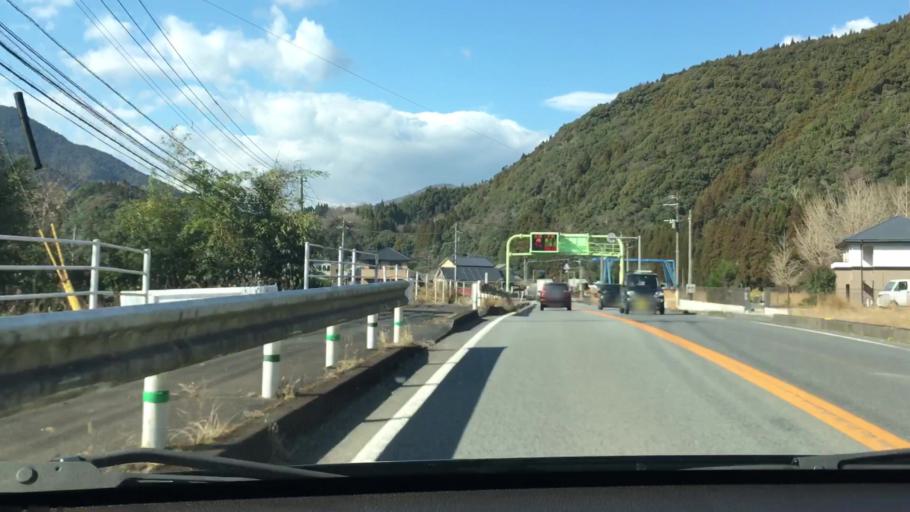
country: JP
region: Oita
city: Saiki
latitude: 32.9869
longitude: 131.8388
